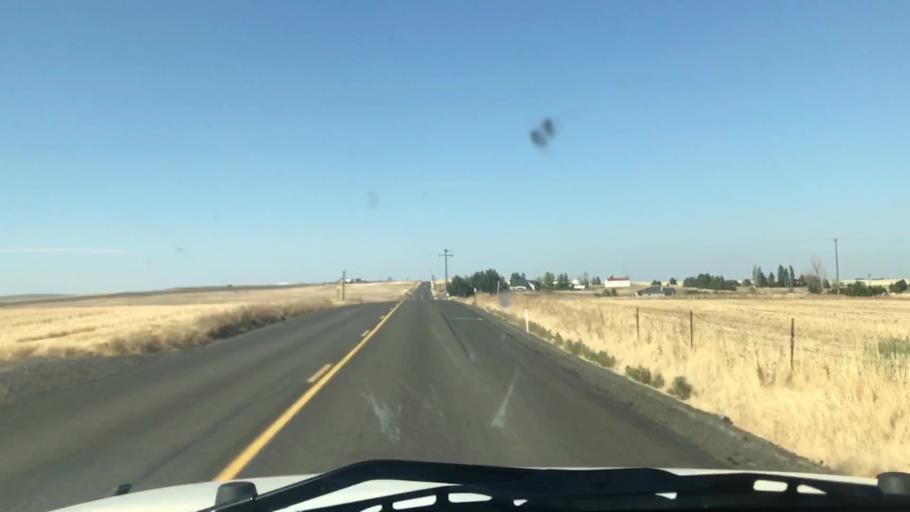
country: US
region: Washington
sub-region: Spokane County
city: Fairchild Air Force Base
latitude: 47.6568
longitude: -117.7331
